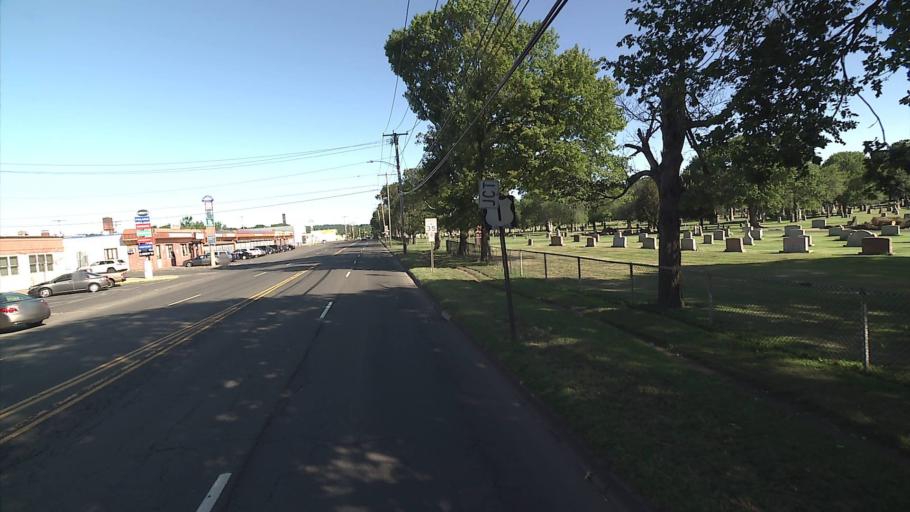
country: US
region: Connecticut
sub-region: New Haven County
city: New Haven
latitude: 41.2951
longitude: -72.9462
